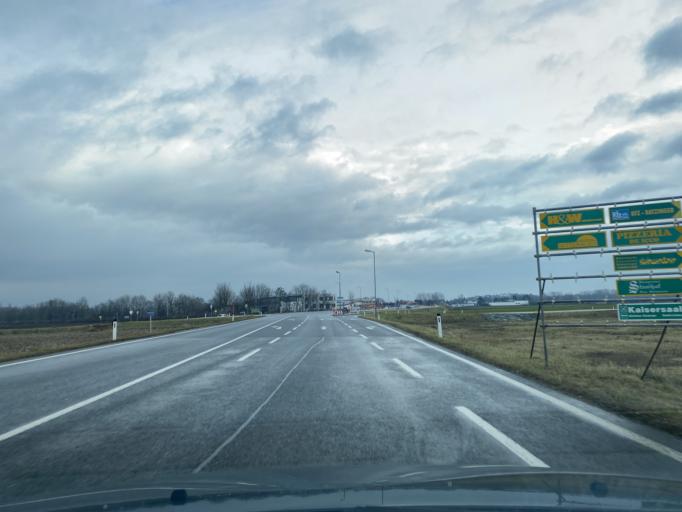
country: AT
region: Lower Austria
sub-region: Politischer Bezirk Sankt Polten
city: Hafnerbach
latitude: 48.1995
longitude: 15.4946
